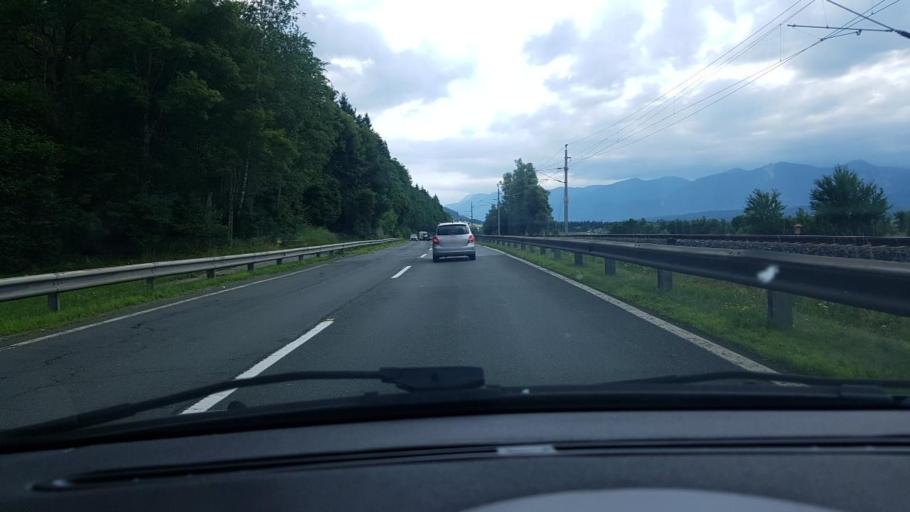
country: AT
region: Carinthia
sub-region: Politischer Bezirk Villach Land
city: Feistritz an der Gail
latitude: 46.5951
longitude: 13.5990
